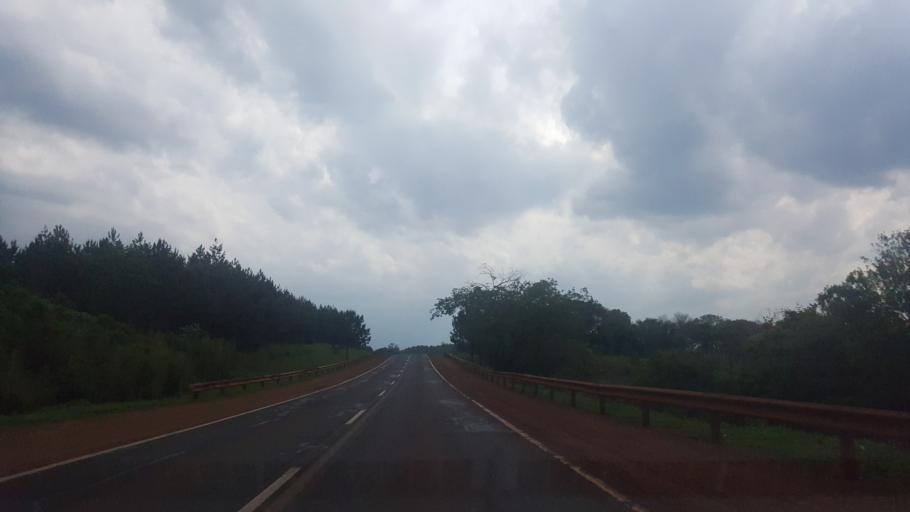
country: AR
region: Misiones
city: Santo Pipo
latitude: -27.1126
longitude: -55.3514
